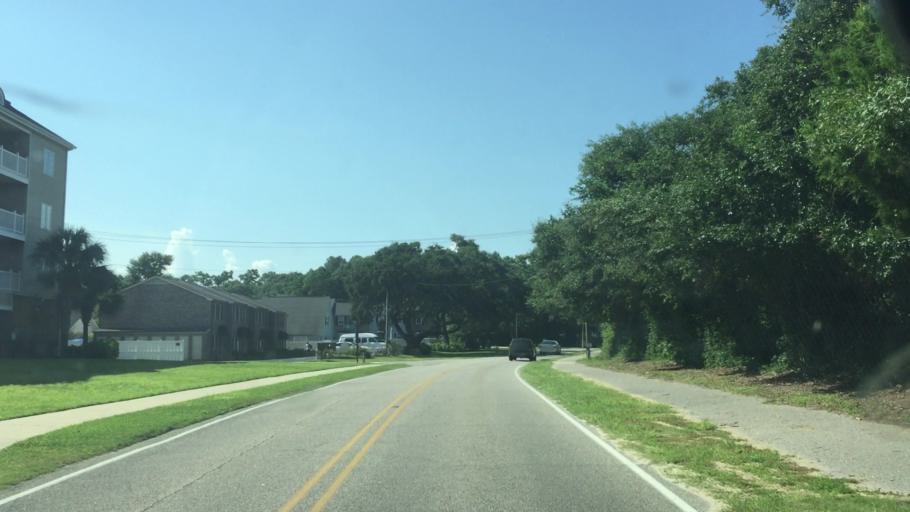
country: US
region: South Carolina
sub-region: Horry County
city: North Myrtle Beach
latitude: 33.8220
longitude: -78.6716
